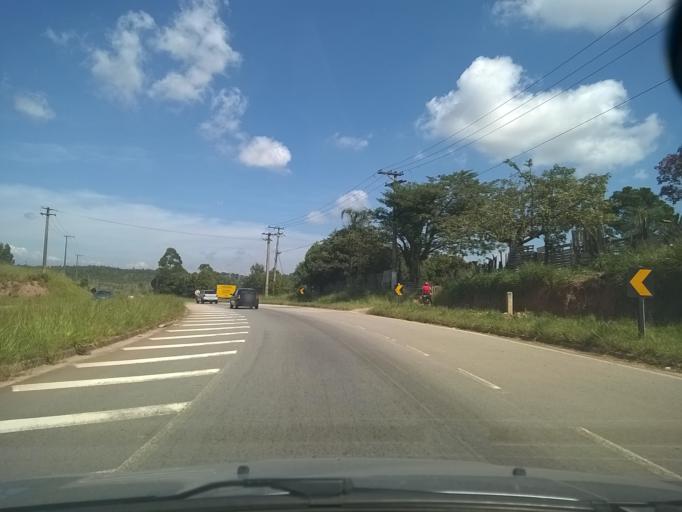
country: BR
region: Sao Paulo
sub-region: Francisco Morato
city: Francisco Morato
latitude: -23.2954
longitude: -46.7684
